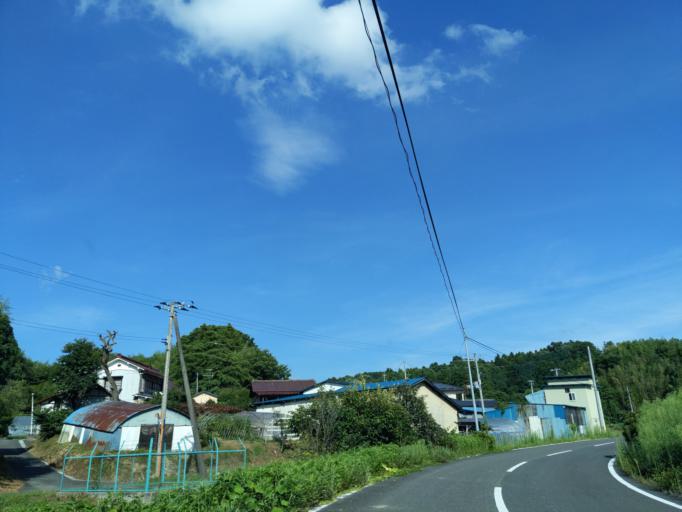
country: JP
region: Fukushima
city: Koriyama
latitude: 37.4035
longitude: 140.4287
